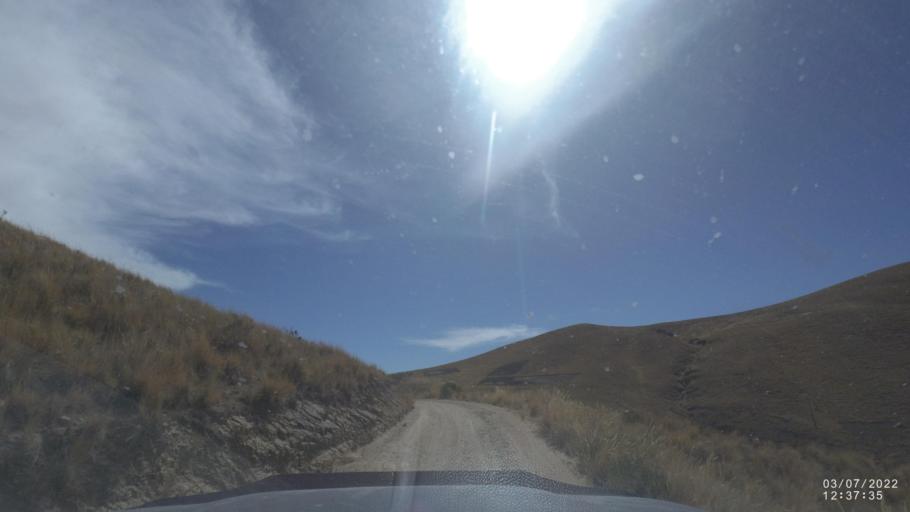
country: BO
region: Cochabamba
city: Irpa Irpa
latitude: -17.7969
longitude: -66.6159
